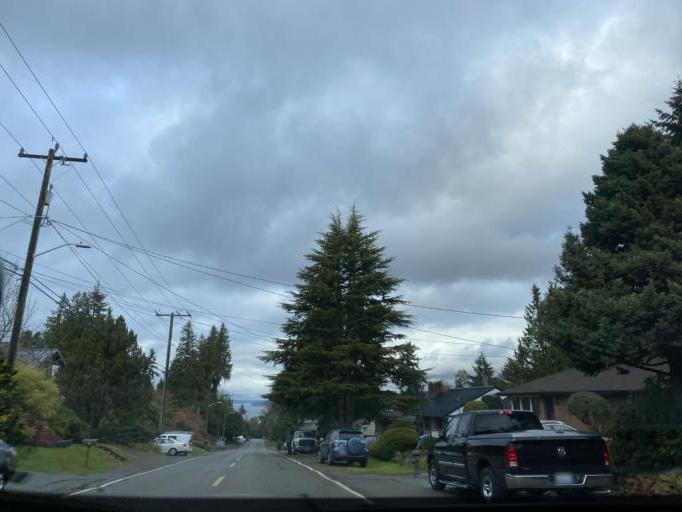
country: US
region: Washington
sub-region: King County
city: Shoreline
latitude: 47.6928
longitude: -122.3929
